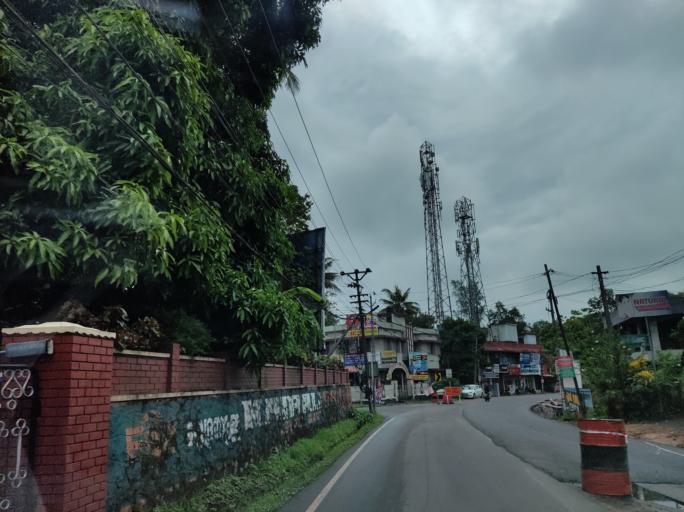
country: IN
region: Kerala
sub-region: Alappuzha
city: Mavelikara
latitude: 9.2493
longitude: 76.5342
